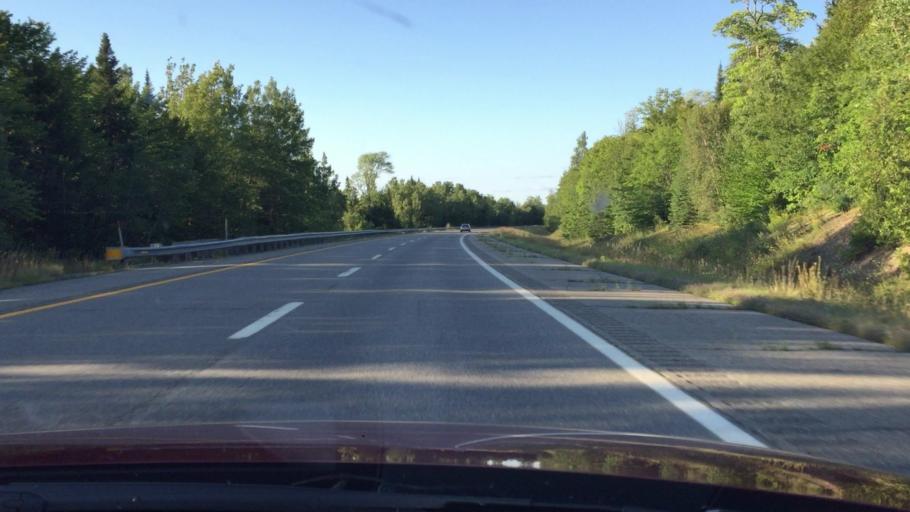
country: US
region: Maine
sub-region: Penobscot County
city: Patten
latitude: 45.8397
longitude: -68.4330
